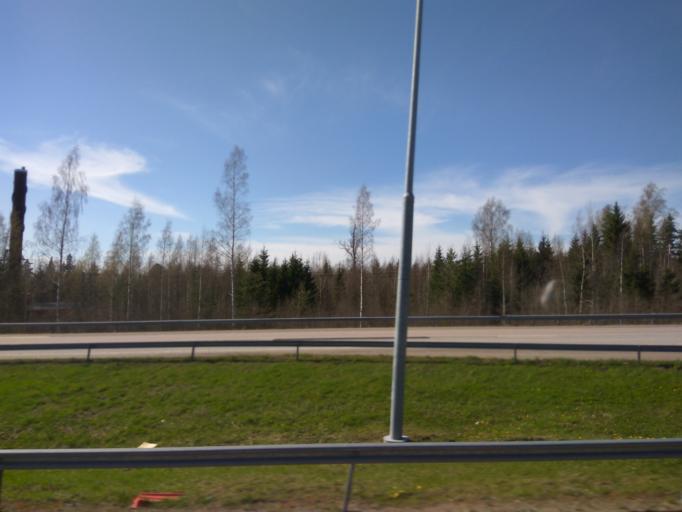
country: FI
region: Uusimaa
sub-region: Porvoo
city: Porvoo
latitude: 60.3964
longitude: 25.6225
